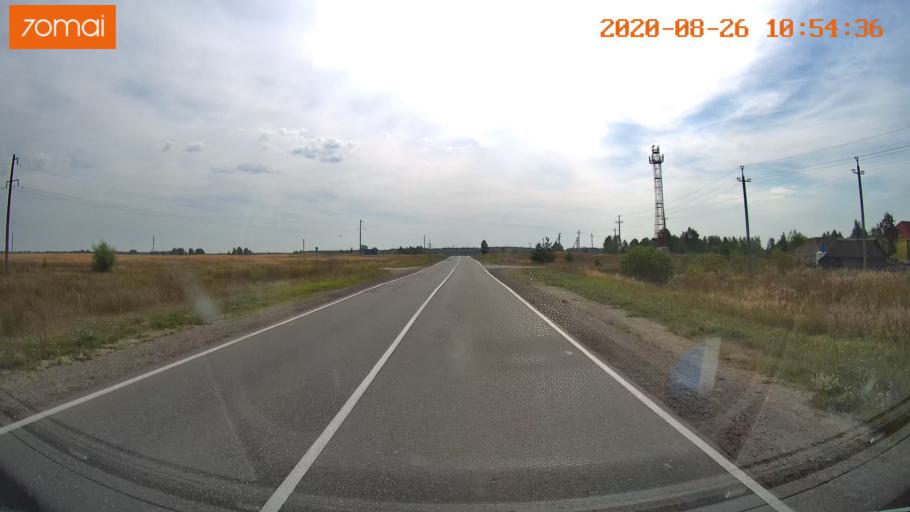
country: RU
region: Rjazan
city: Izhevskoye
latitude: 54.6261
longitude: 41.1656
